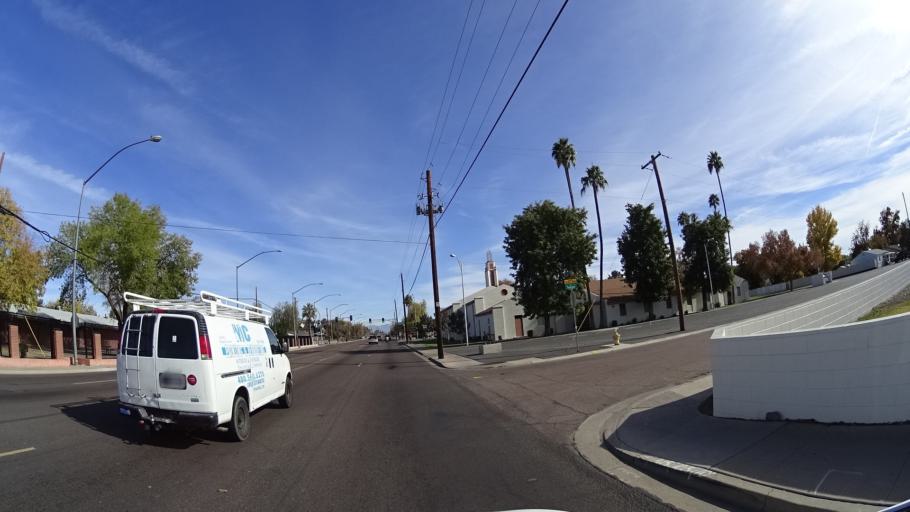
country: US
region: Arizona
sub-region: Maricopa County
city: Mesa
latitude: 33.4078
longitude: -111.8110
